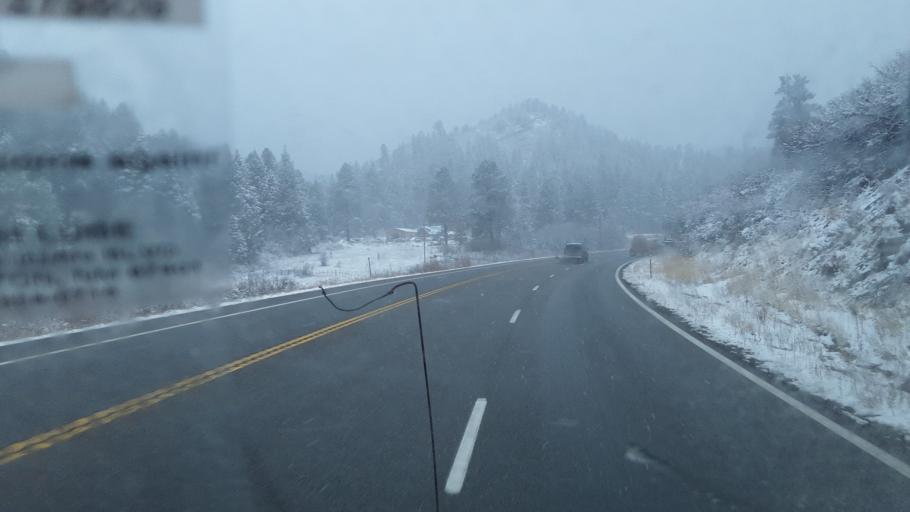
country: US
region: Colorado
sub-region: La Plata County
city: Bayfield
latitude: 37.2278
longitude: -107.4101
